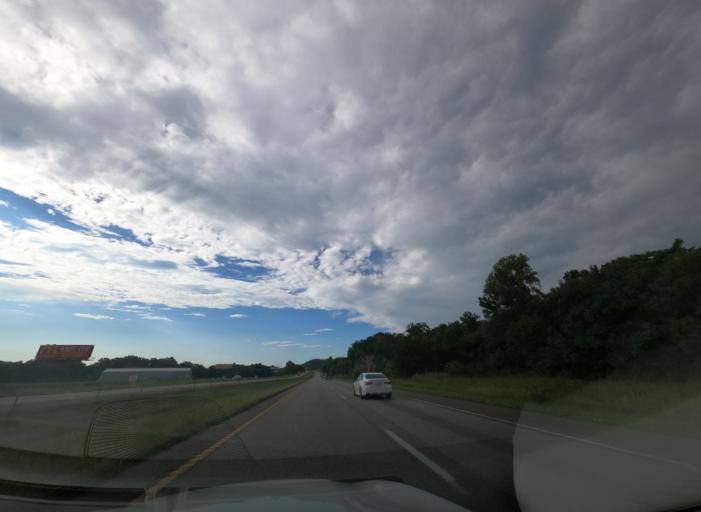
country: US
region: Missouri
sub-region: Sainte Genevieve County
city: Sainte Genevieve
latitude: 38.0128
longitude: -90.2282
